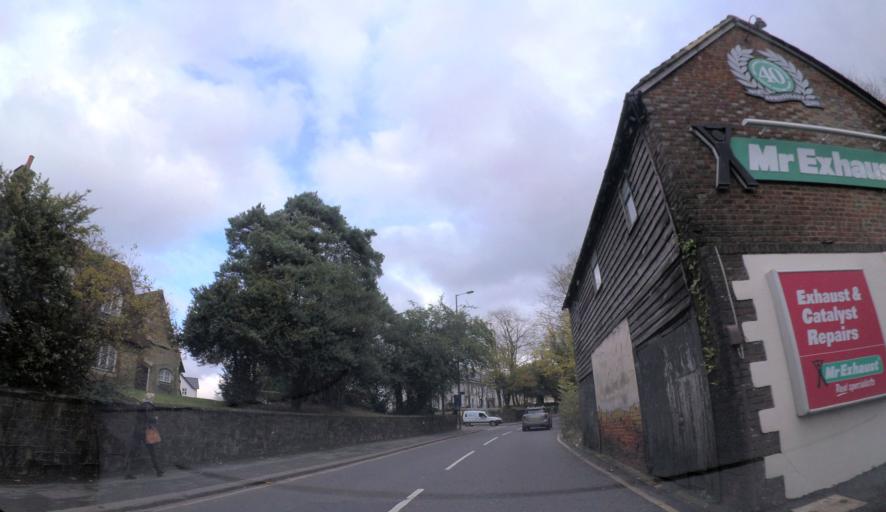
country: GB
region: England
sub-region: Surrey
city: Reigate
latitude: 51.2387
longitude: -0.2095
